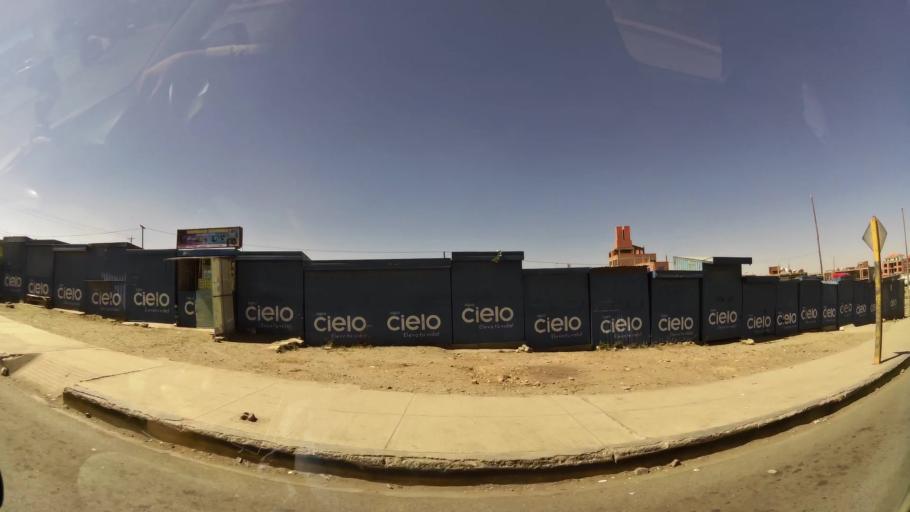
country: BO
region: La Paz
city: La Paz
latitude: -16.5147
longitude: -68.2185
